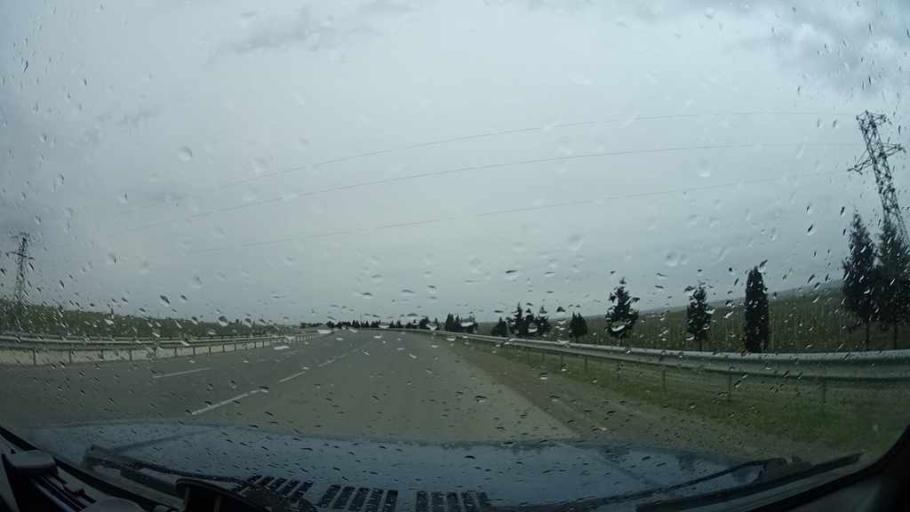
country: AZ
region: Goygol Rayon
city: Yelenendorf
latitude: 40.6029
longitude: 46.3429
